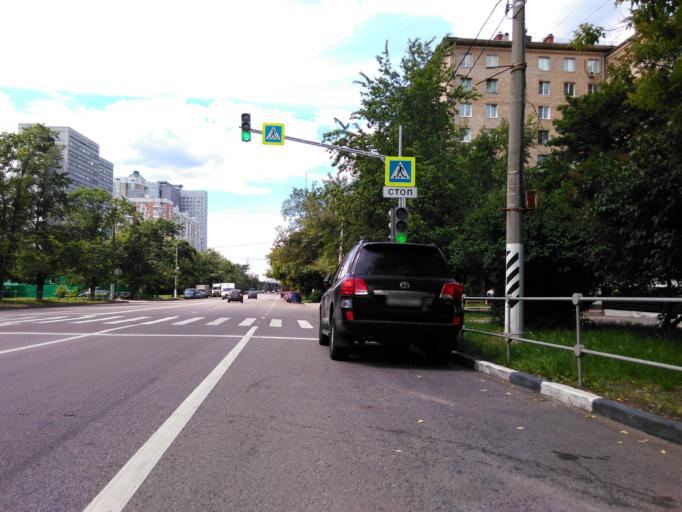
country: RU
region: Moscow
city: Ramenki
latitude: 55.6760
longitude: 37.5194
